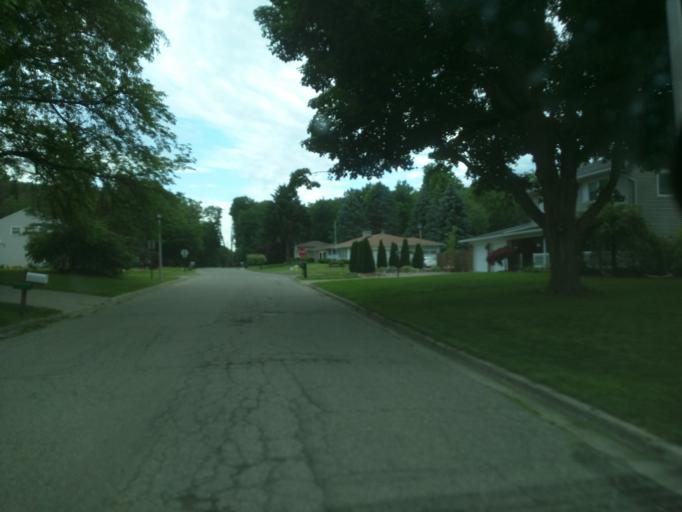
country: US
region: Michigan
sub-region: Eaton County
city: Waverly
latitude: 42.7501
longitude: -84.6170
